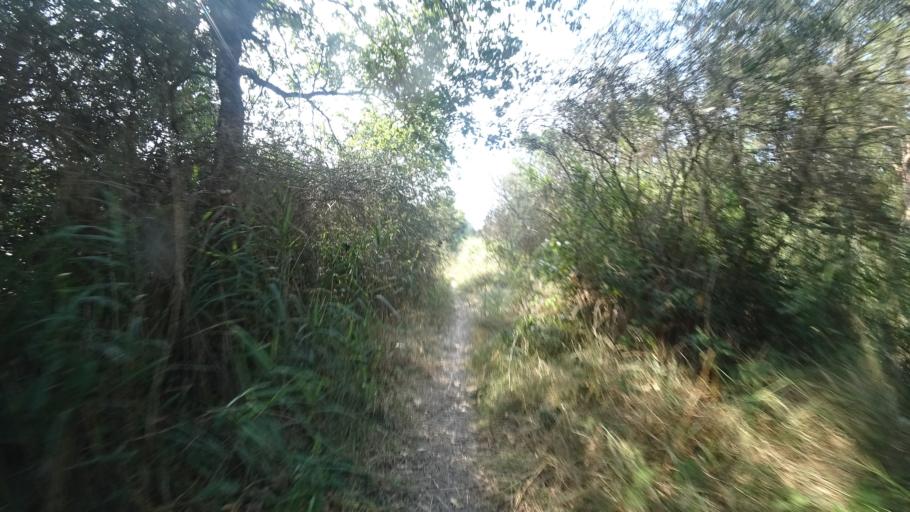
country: FR
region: Languedoc-Roussillon
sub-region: Departement des Pyrenees-Orientales
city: Canet-en-Roussillon
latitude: 42.6902
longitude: 3.0262
